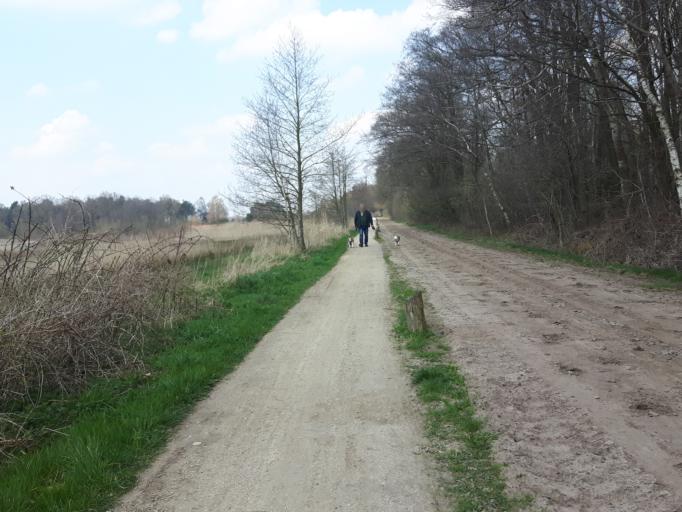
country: NL
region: Overijssel
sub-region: Gemeente Haaksbergen
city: Haaksbergen
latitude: 52.1574
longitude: 6.8134
